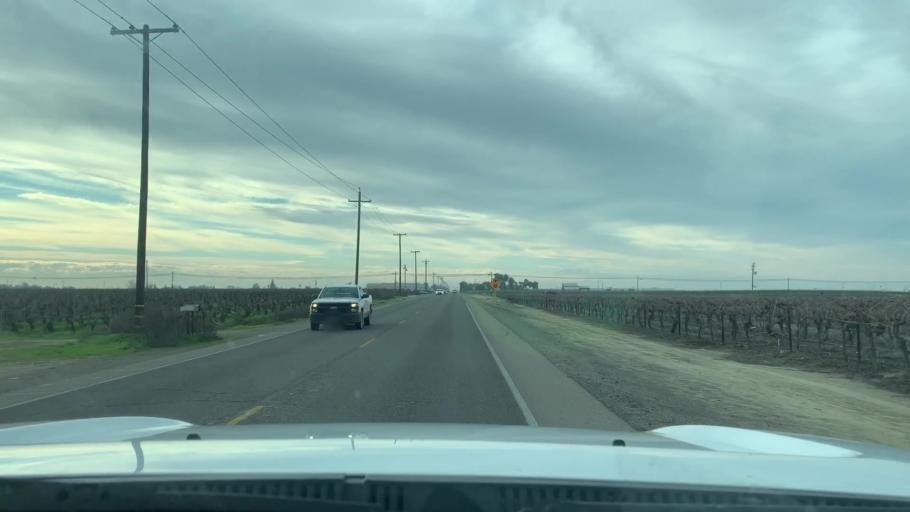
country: US
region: California
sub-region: Fresno County
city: Fowler
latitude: 36.6055
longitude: -119.7341
